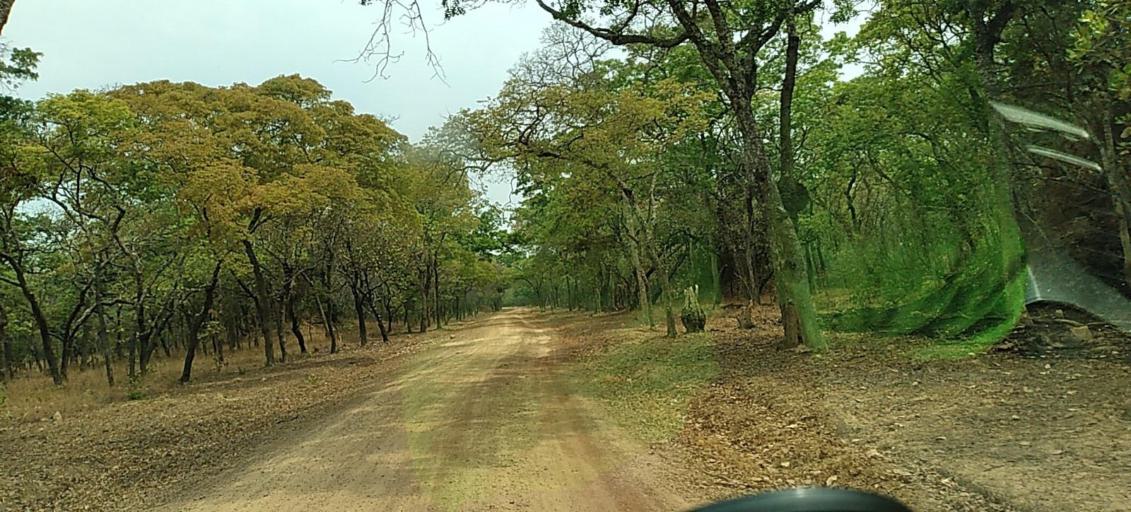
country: ZM
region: North-Western
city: Solwezi
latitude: -12.9362
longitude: 26.5591
